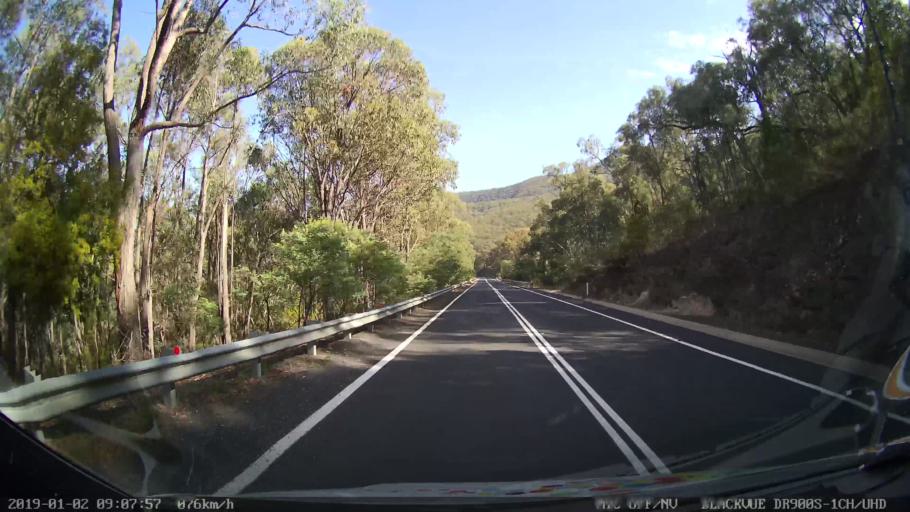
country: AU
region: New South Wales
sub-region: Tumut Shire
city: Tumut
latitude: -35.5354
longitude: 148.2952
